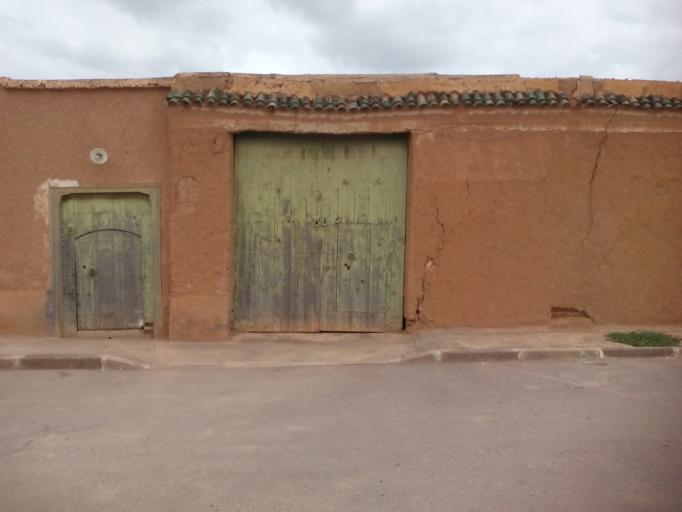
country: MA
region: Marrakech-Tensift-Al Haouz
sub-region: Marrakech
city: Marrakesh
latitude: 31.6711
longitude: -8.3403
